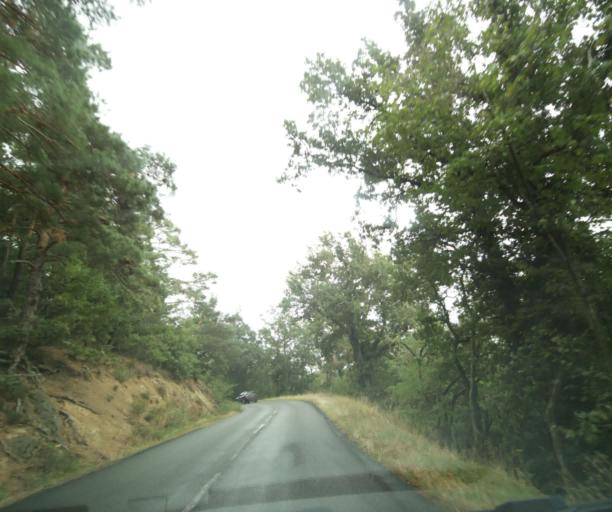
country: FR
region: Auvergne
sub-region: Departement du Puy-de-Dome
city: Durtol
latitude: 45.7938
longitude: 3.0376
